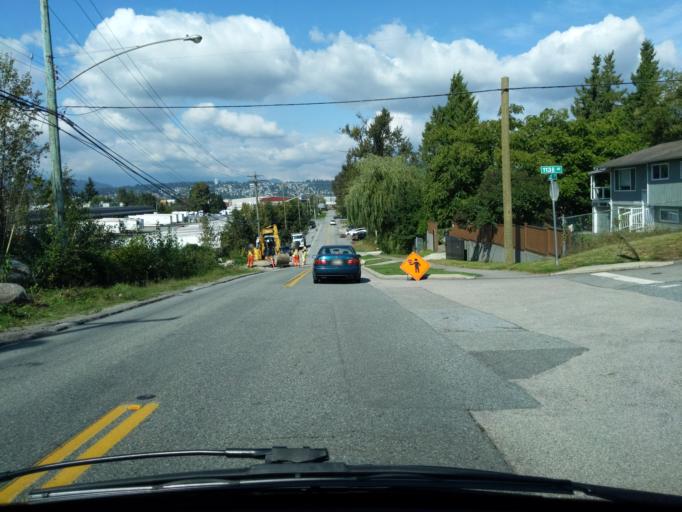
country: CA
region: British Columbia
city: New Westminster
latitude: 49.2090
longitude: -122.8563
